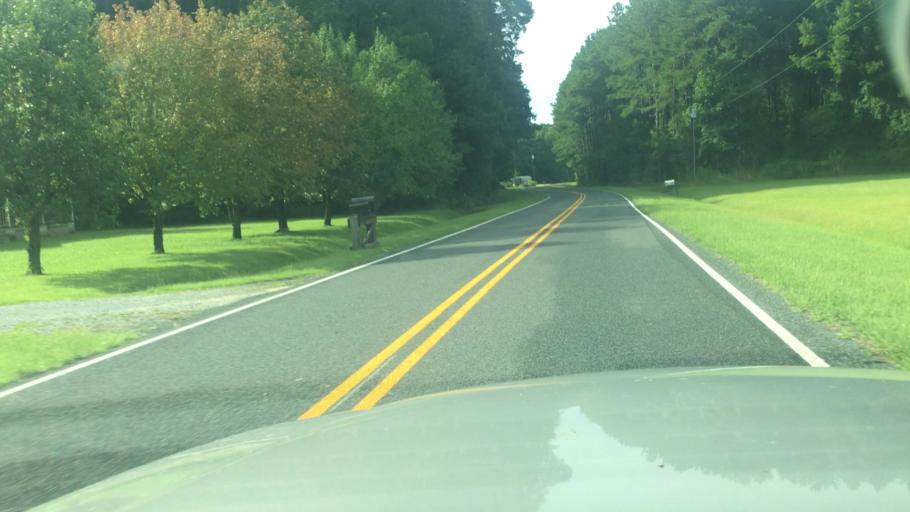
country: US
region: North Carolina
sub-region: Cumberland County
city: Eastover
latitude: 35.1581
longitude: -78.8534
